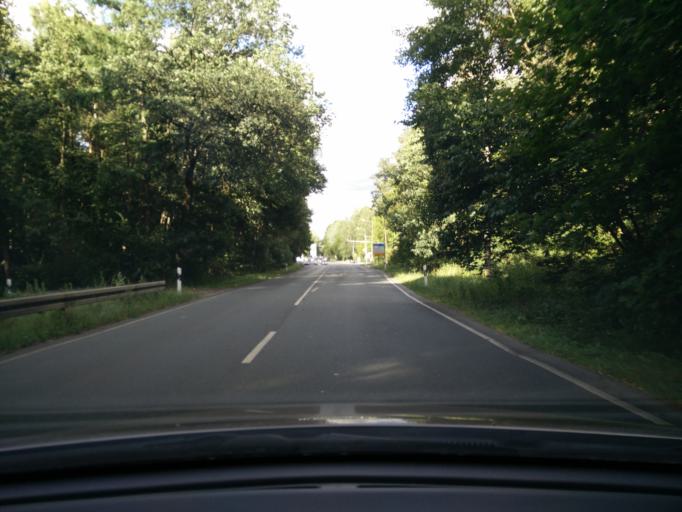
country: DE
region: Bavaria
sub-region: Regierungsbezirk Mittelfranken
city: Wendelstein
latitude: 49.4060
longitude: 11.1617
